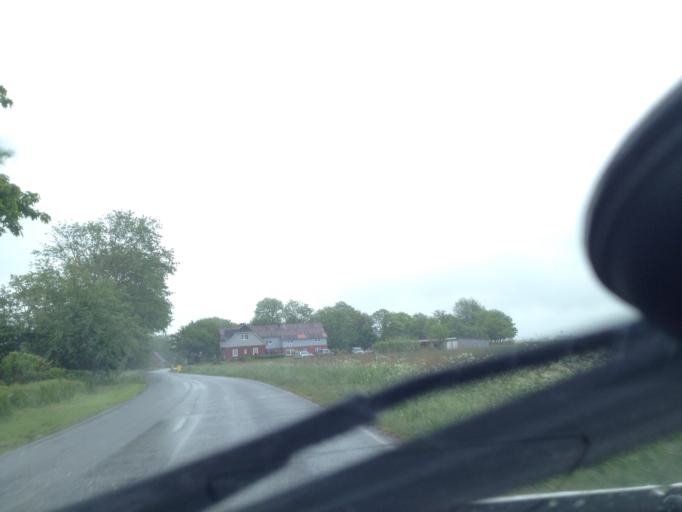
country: DE
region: Schleswig-Holstein
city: Rodenas
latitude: 54.8882
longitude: 8.6965
